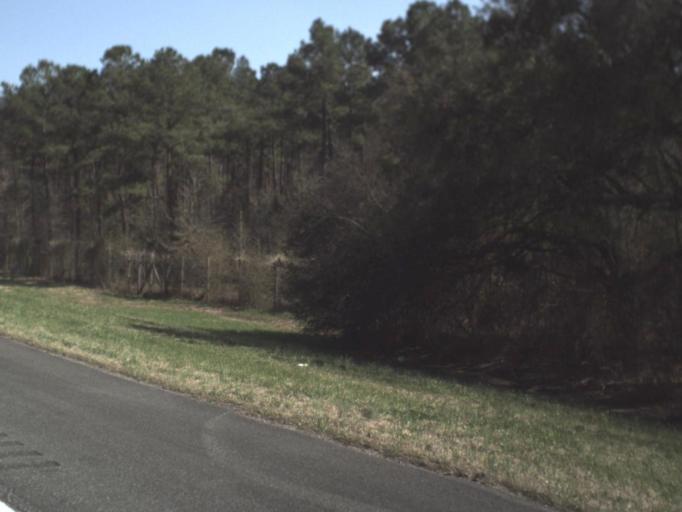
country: US
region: Florida
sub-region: Jackson County
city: Marianna
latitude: 30.7576
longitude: -85.3373
